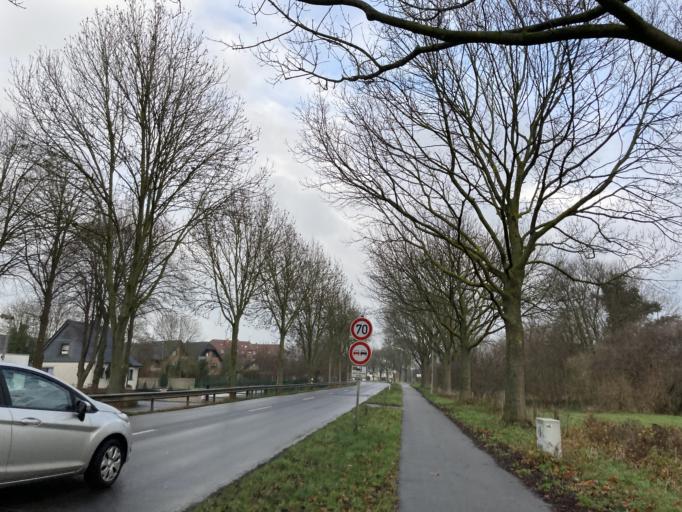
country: DE
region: North Rhine-Westphalia
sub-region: Regierungsbezirk Dusseldorf
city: Neubrueck
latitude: 51.1219
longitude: 6.6262
